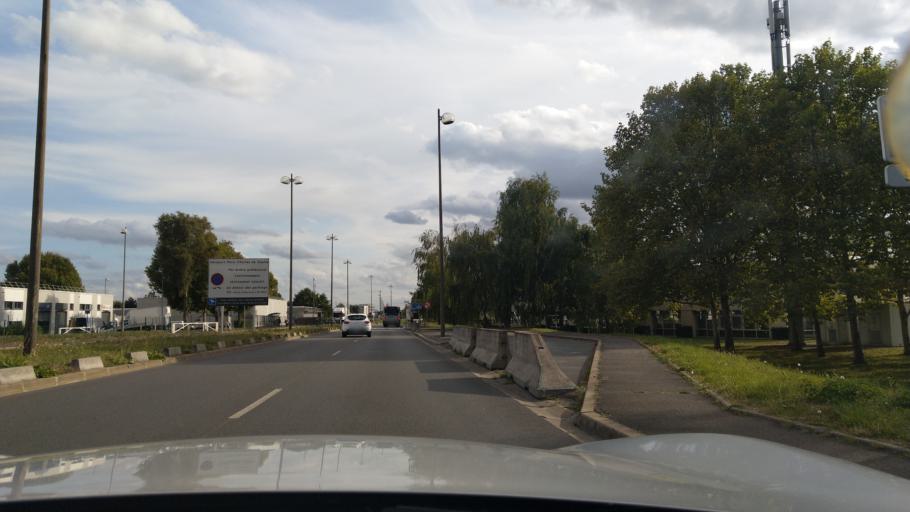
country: FR
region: Ile-de-France
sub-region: Departement du Val-d'Oise
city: Roissy-en-France
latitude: 48.9957
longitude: 2.5235
